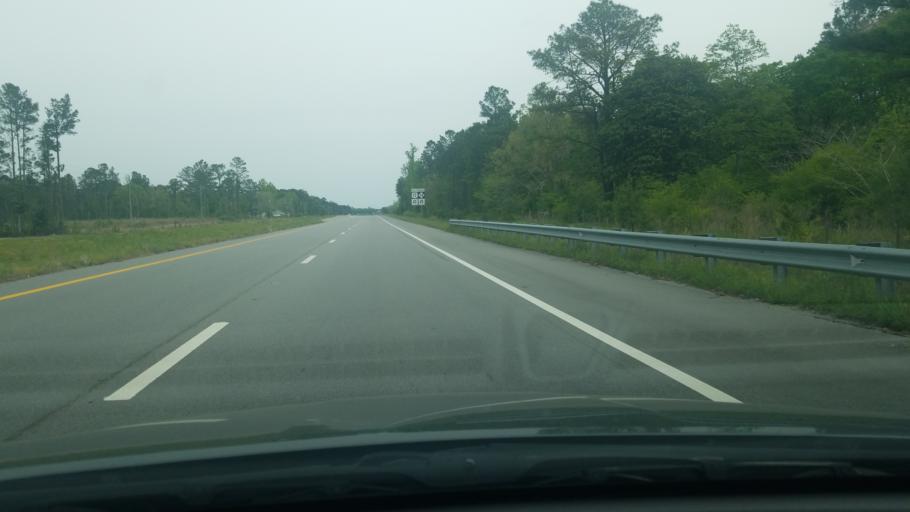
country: US
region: North Carolina
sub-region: Jones County
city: Maysville
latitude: 34.9593
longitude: -77.2414
